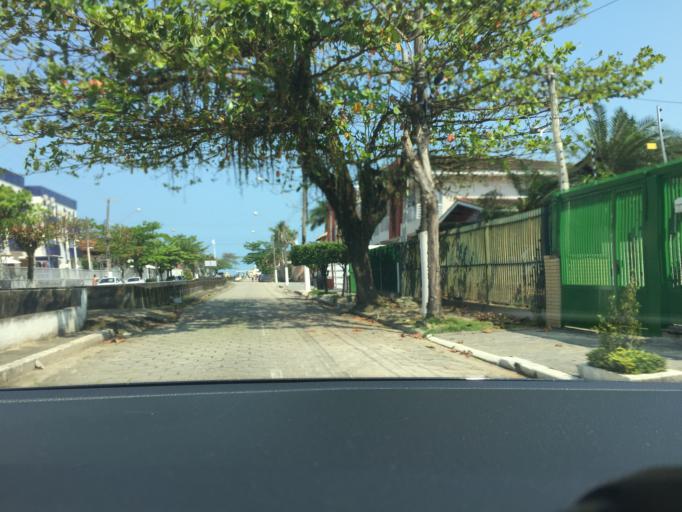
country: BR
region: Sao Paulo
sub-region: Guaruja
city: Guaruja
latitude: -23.9831
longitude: -46.2213
